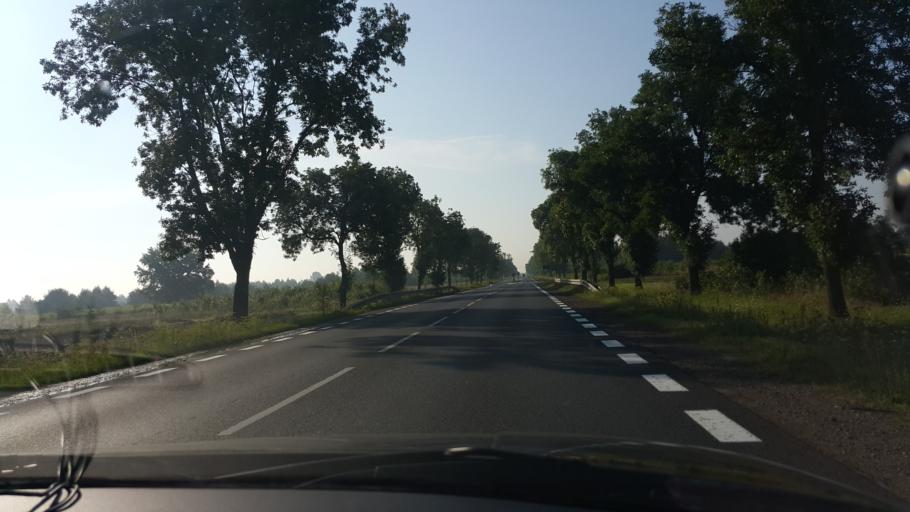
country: PL
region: Masovian Voivodeship
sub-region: Powiat radomski
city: Jedlnia-Letnisko
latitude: 51.3996
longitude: 21.2576
